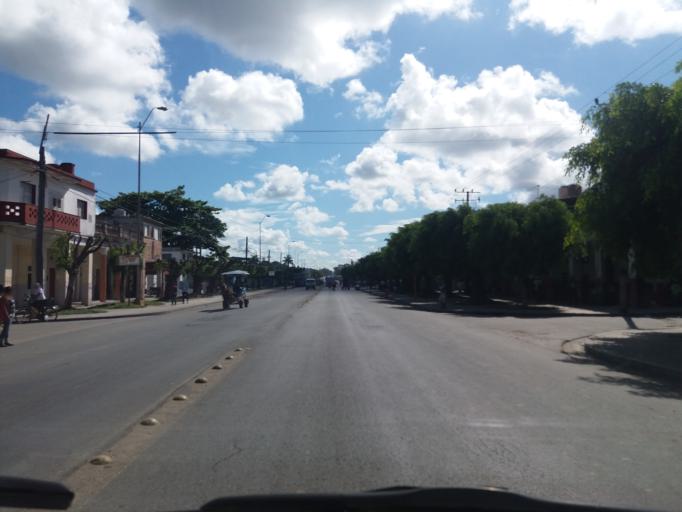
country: CU
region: Cienfuegos
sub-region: Municipio de Cienfuegos
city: Cienfuegos
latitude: 22.1516
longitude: -80.4400
